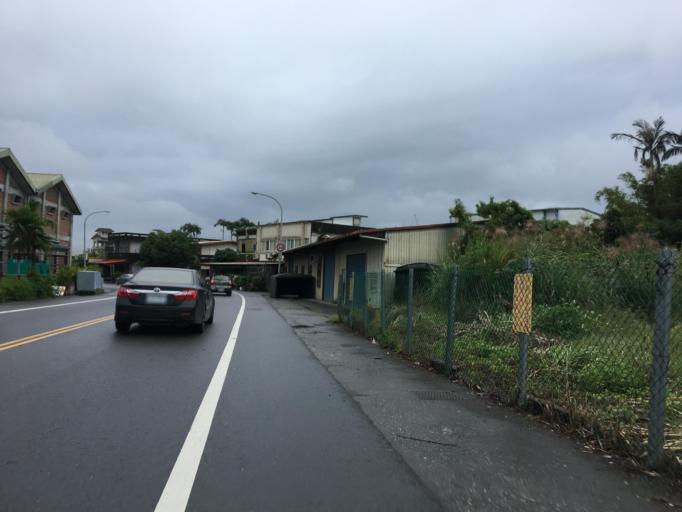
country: TW
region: Taiwan
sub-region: Yilan
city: Yilan
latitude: 24.6555
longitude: 121.7613
